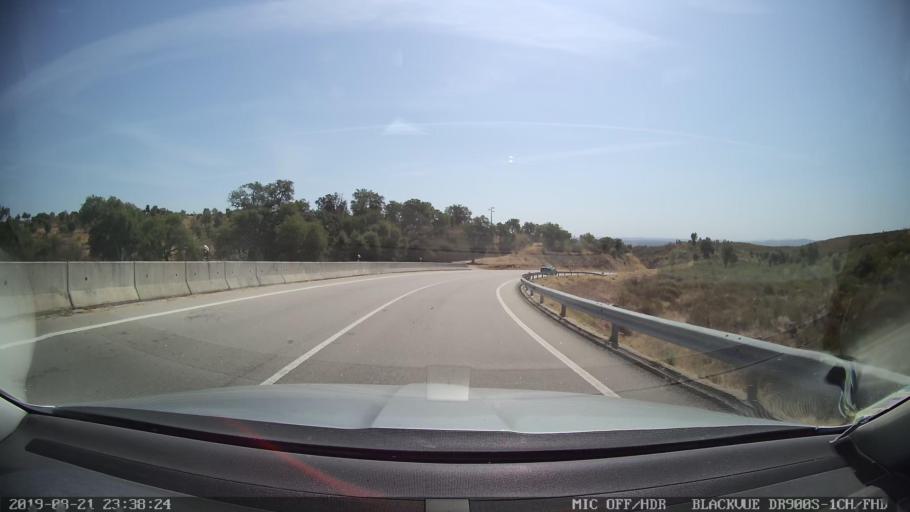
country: PT
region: Guarda
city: Alcains
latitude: 39.8613
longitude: -7.3516
